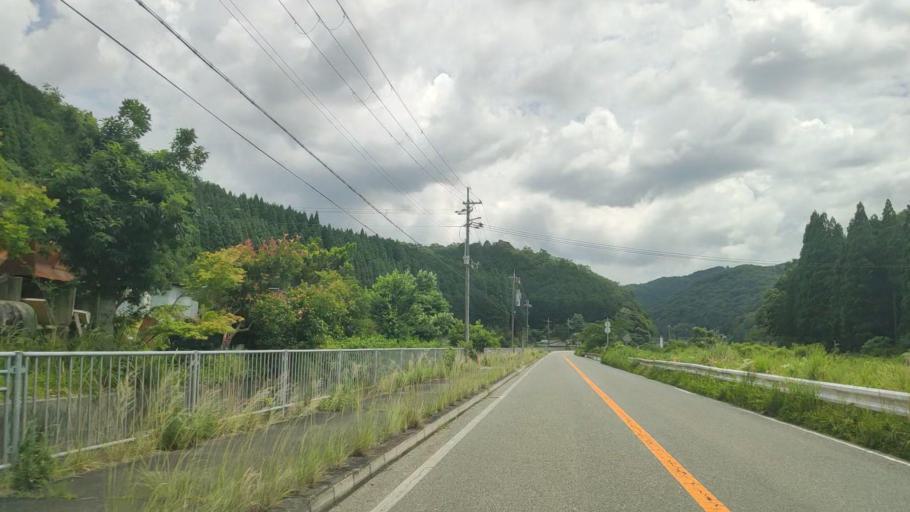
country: JP
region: Hyogo
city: Yamazakicho-nakabirose
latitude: 34.9702
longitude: 134.4472
